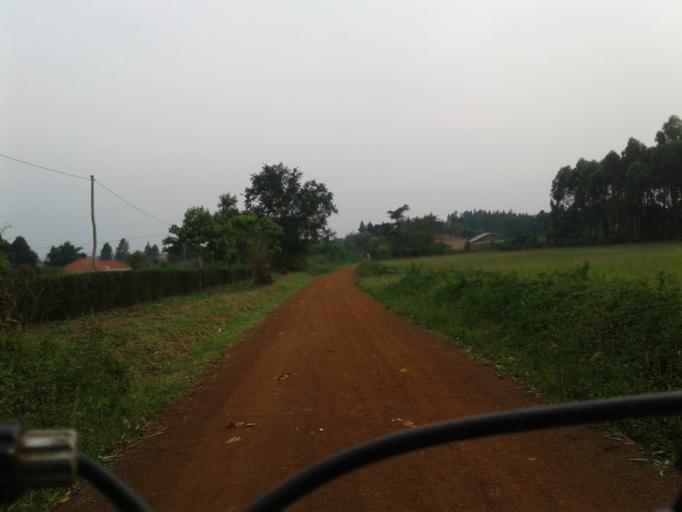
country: UG
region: Western Region
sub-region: Hoima District
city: Hoima
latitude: 1.4228
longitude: 31.3230
